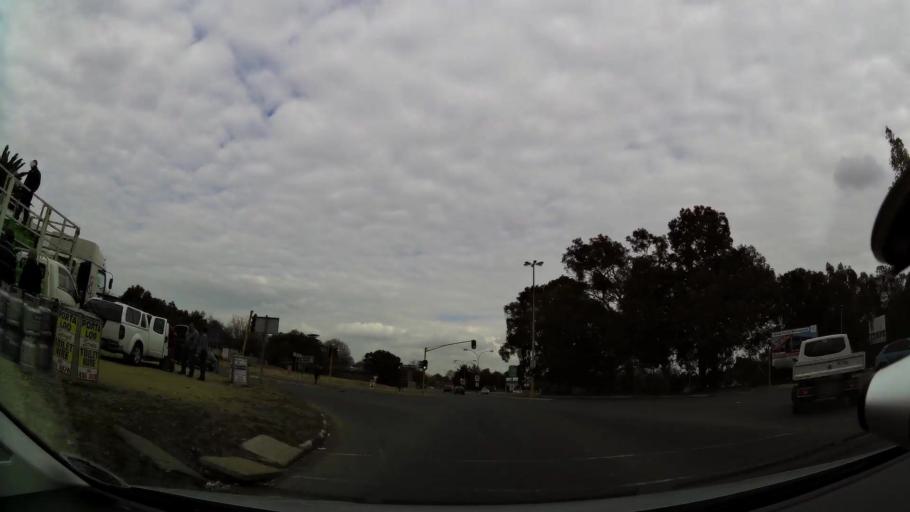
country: ZA
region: Orange Free State
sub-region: Mangaung Metropolitan Municipality
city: Bloemfontein
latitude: -29.0963
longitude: 26.2033
